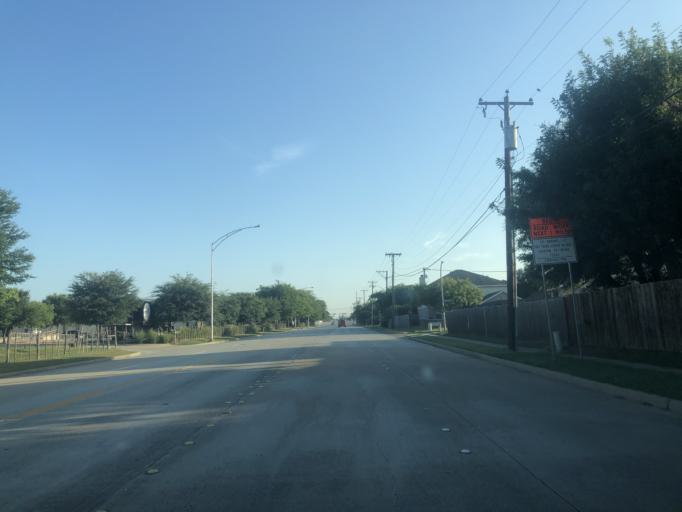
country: US
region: Texas
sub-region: Tarrant County
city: White Settlement
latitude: 32.7250
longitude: -97.5038
